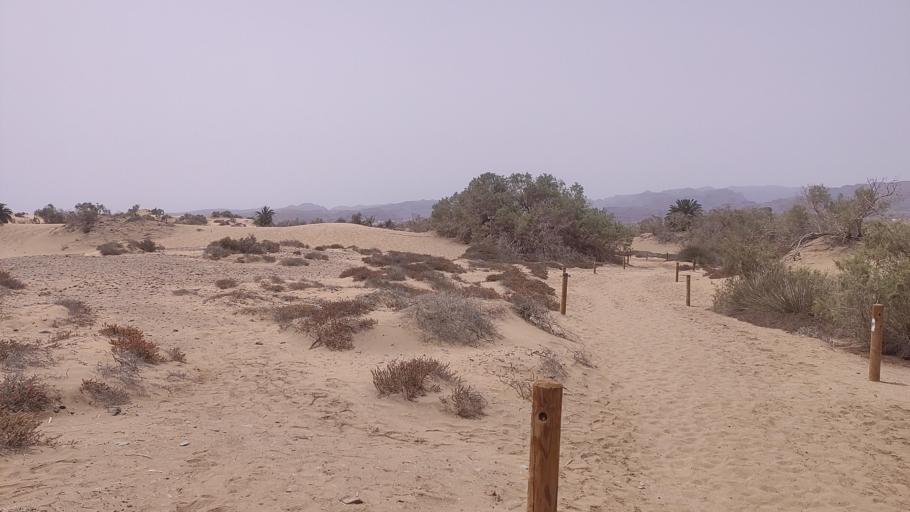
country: ES
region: Canary Islands
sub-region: Provincia de Las Palmas
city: Playa del Ingles
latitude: 27.7393
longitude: -15.5882
